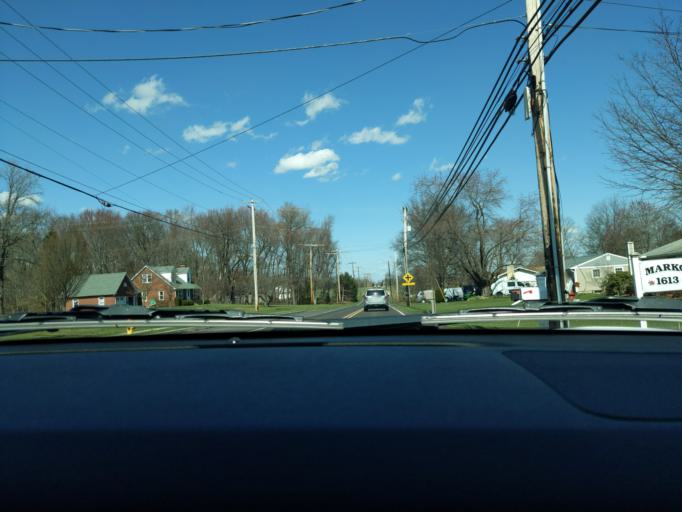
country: US
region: Pennsylvania
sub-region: Bucks County
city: Perkasie
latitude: 40.3922
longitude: -75.2666
